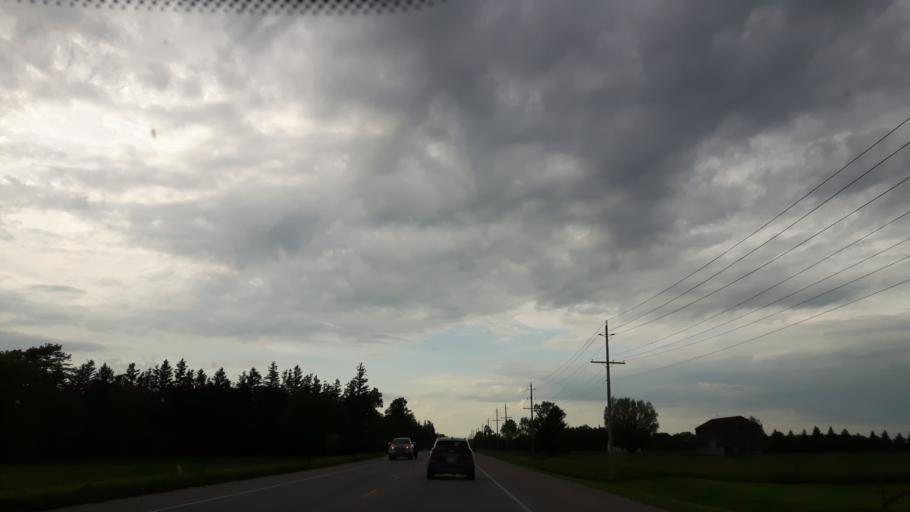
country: CA
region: Ontario
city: South Huron
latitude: 43.4024
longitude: -81.4920
